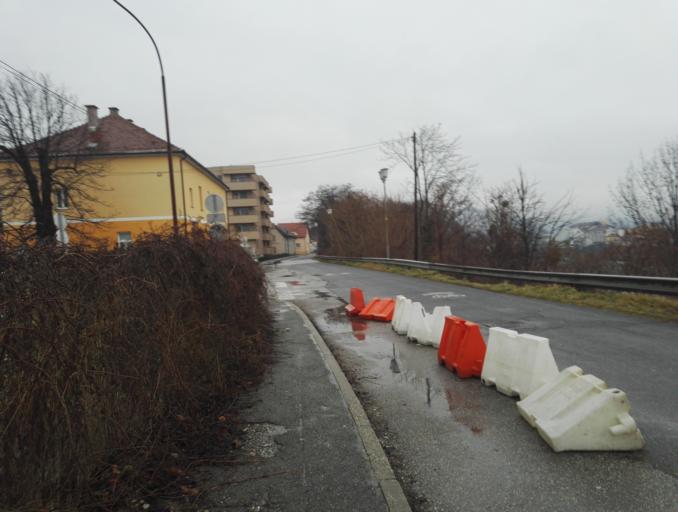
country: SI
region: Maribor
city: Maribor
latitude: 46.5559
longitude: 15.6360
